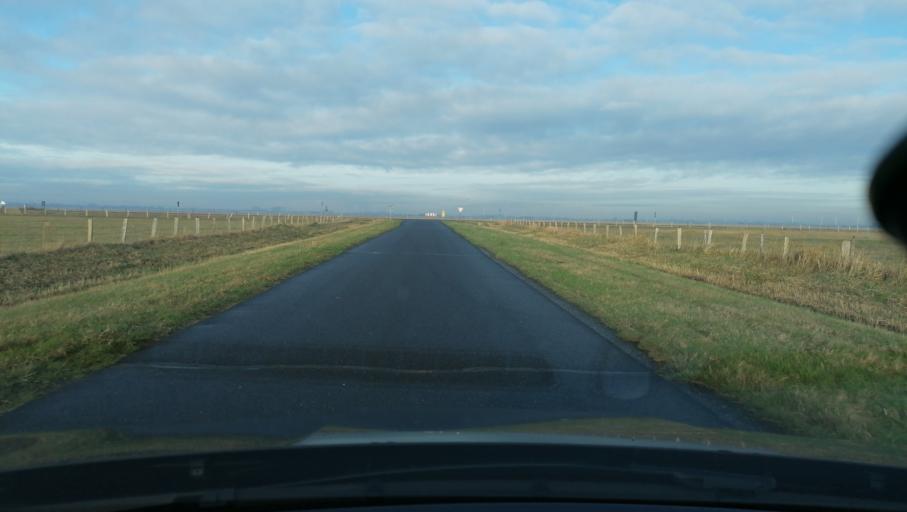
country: DE
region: Schleswig-Holstein
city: Friedrichsgabekoog
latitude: 54.1152
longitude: 8.9519
